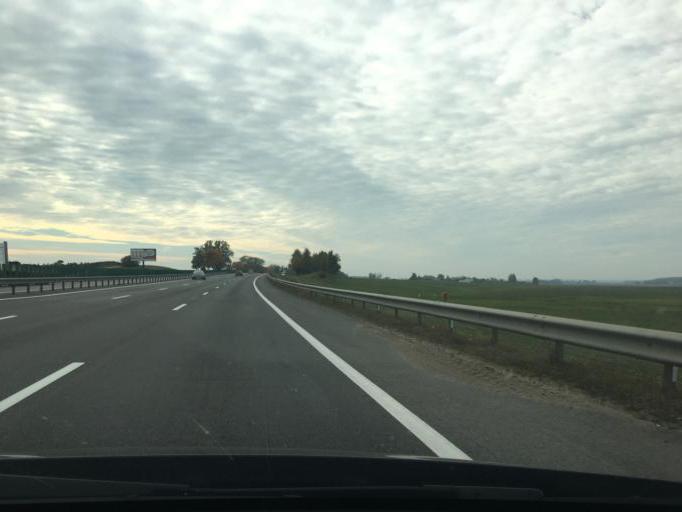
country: BY
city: Fanipol
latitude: 53.7343
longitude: 27.3014
